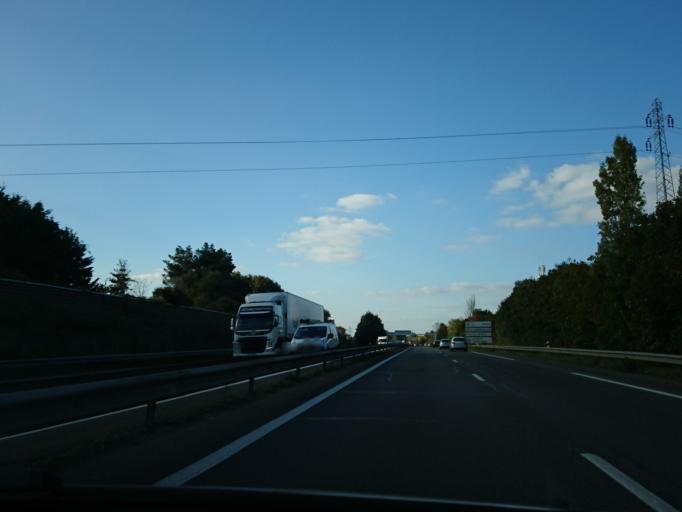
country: FR
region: Pays de la Loire
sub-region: Departement de la Loire-Atlantique
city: Orvault
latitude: 47.2700
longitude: -1.5914
